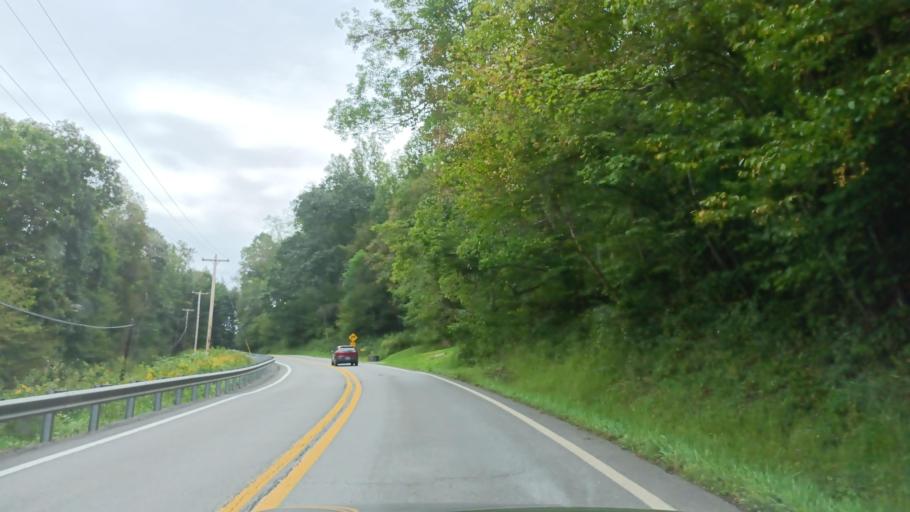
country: US
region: West Virginia
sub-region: Taylor County
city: Grafton
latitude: 39.3326
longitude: -79.9044
